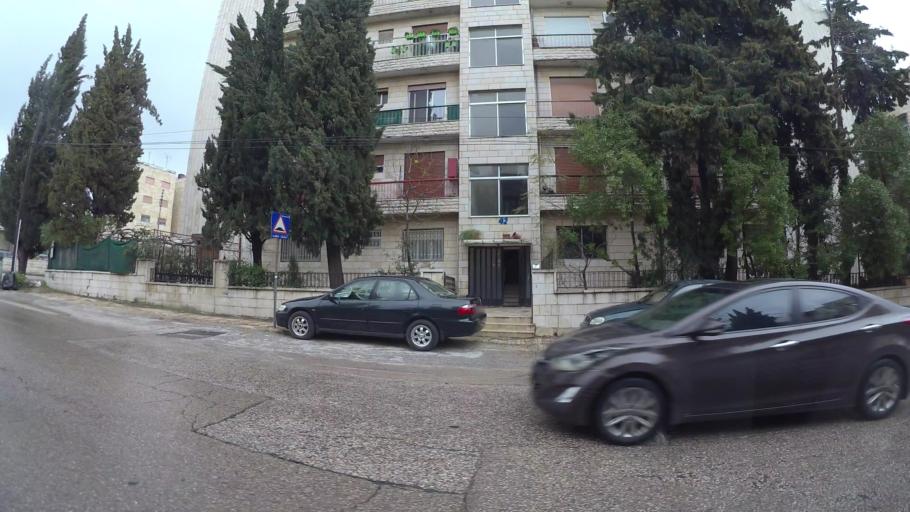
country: JO
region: Amman
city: Wadi as Sir
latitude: 31.9543
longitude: 35.8686
